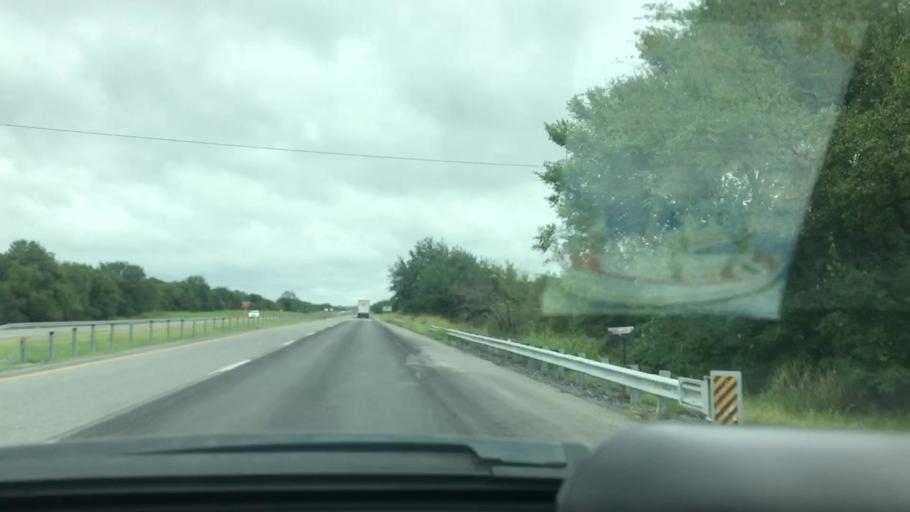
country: US
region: Oklahoma
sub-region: Pittsburg County
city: McAlester
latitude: 34.7999
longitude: -95.8684
